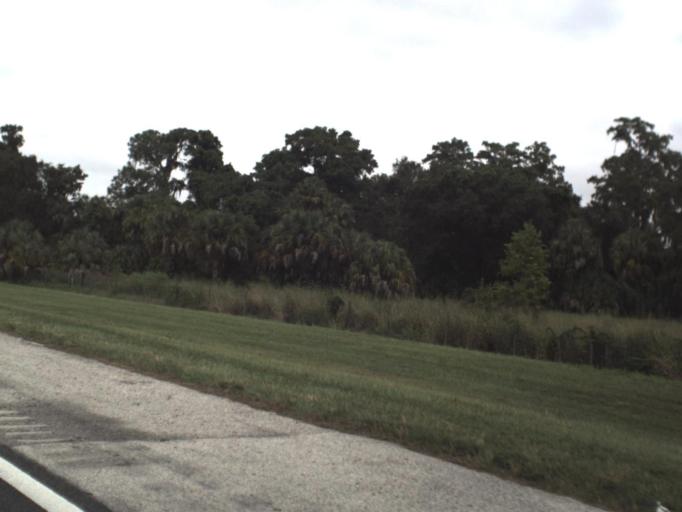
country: US
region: Florida
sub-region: Manatee County
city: Ellenton
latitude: 27.5009
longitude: -82.4775
